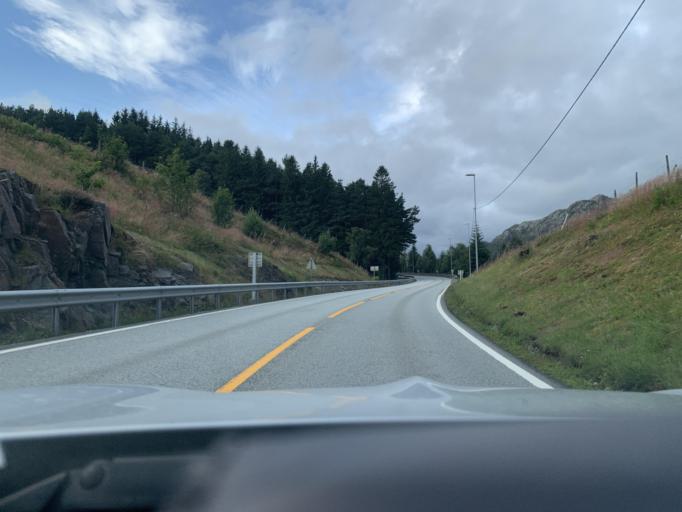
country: NO
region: Rogaland
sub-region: Bjerkreim
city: Vikesa
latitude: 58.6372
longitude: 6.0819
